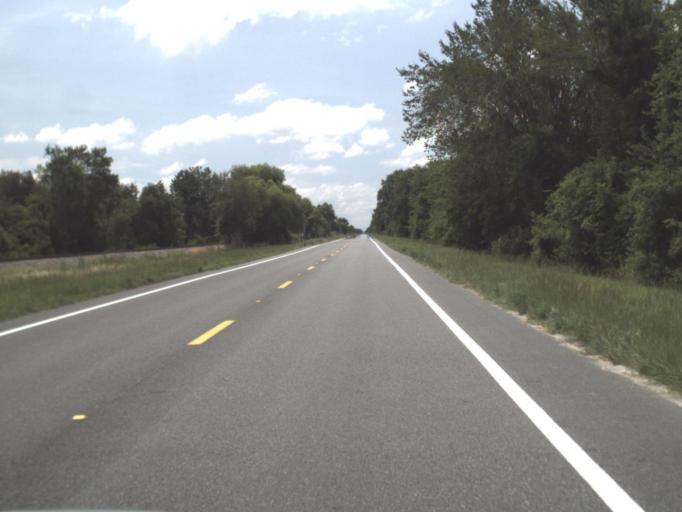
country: US
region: Florida
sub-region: Hamilton County
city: Jasper
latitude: 30.4590
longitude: -82.8951
